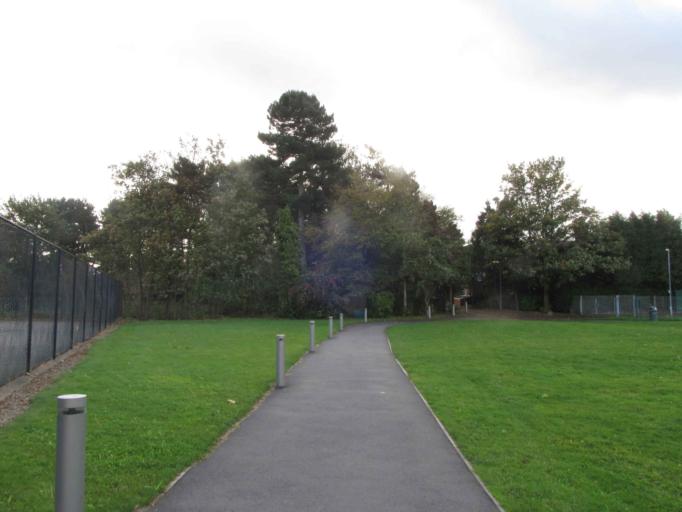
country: GB
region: England
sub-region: Nottingham
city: Nottingham
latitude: 52.9489
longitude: -1.1855
